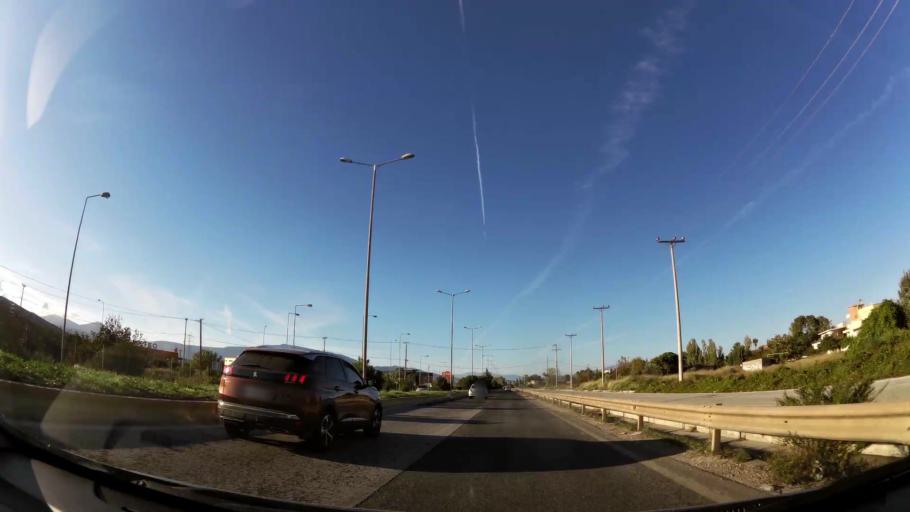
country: GR
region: Attica
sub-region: Nomarchia Anatolikis Attikis
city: Markopoulo
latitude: 37.8798
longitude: 23.9278
